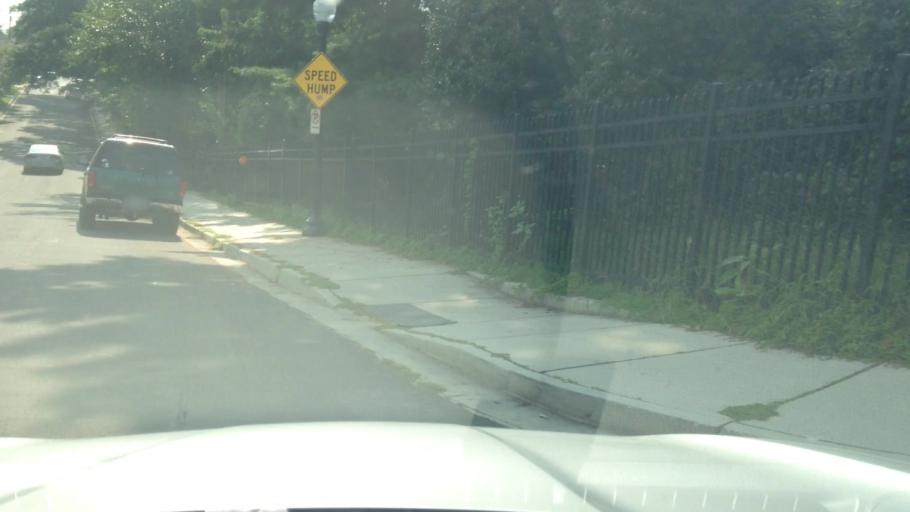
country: US
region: Virginia
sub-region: Fairfax County
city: Seven Corners
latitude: 38.9000
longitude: -77.1392
